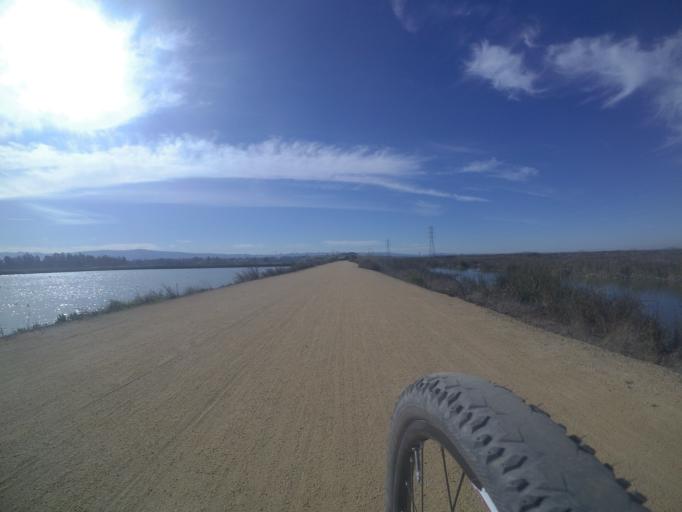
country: US
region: California
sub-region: Santa Clara County
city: Sunnyvale
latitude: 37.4171
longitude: -121.9917
